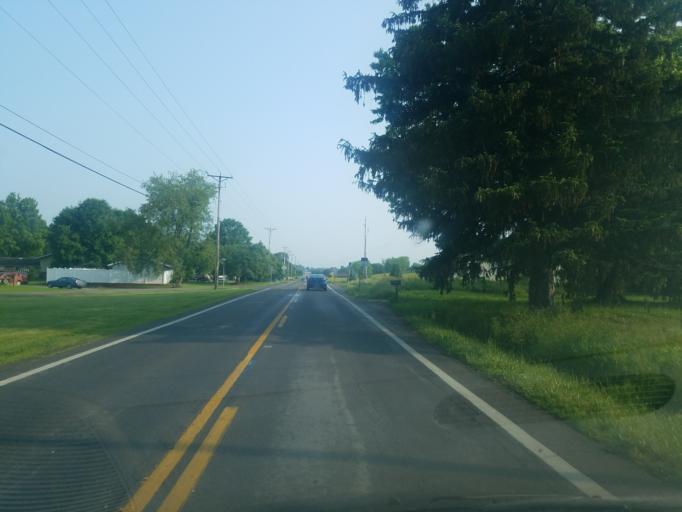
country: US
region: Ohio
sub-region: Tuscarawas County
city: Strasburg
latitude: 40.6233
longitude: -81.4340
